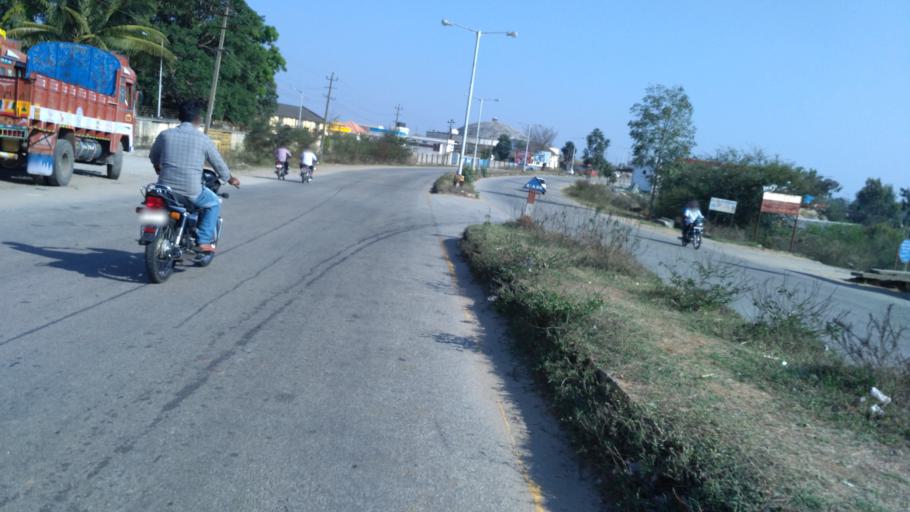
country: IN
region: Karnataka
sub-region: Hassan
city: Hassan
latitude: 12.9716
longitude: 76.1194
